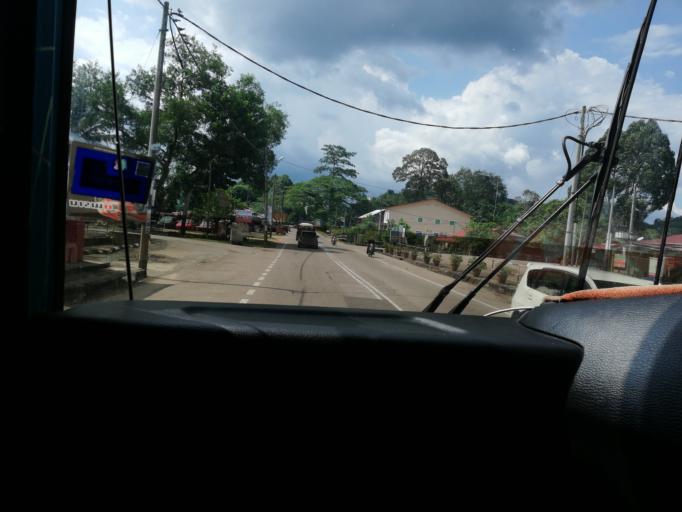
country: MY
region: Penang
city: Nibong Tebal
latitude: 5.2145
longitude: 100.6116
